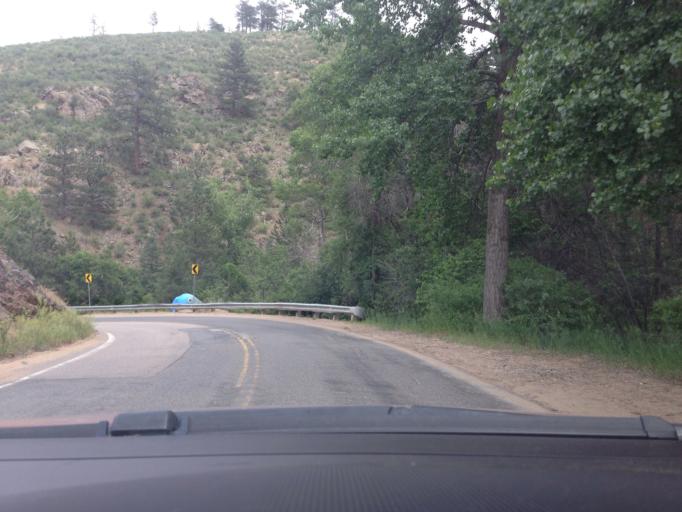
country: US
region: Colorado
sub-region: Larimer County
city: Laporte
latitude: 40.6261
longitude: -105.2194
